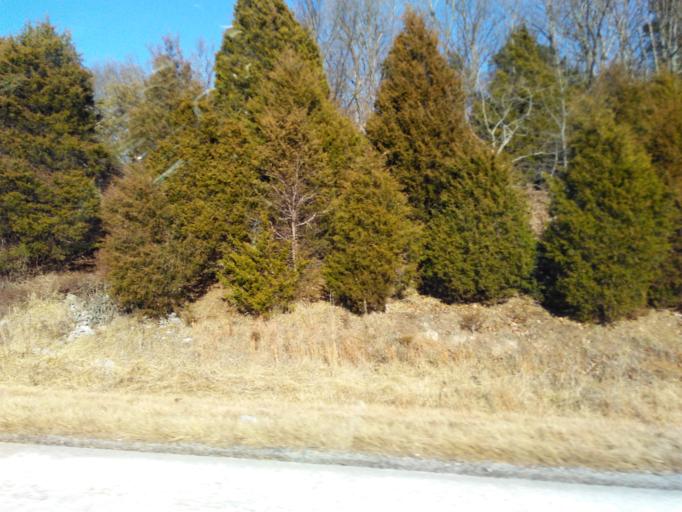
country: US
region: Illinois
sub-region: Johnson County
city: Goreville
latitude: 37.5182
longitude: -88.9119
